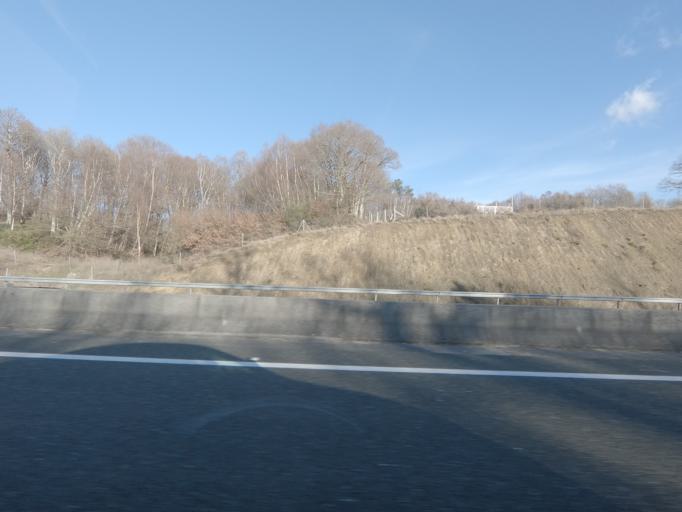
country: ES
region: Galicia
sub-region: Provincia de Pontevedra
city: Lalin
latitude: 42.6423
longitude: -8.1325
